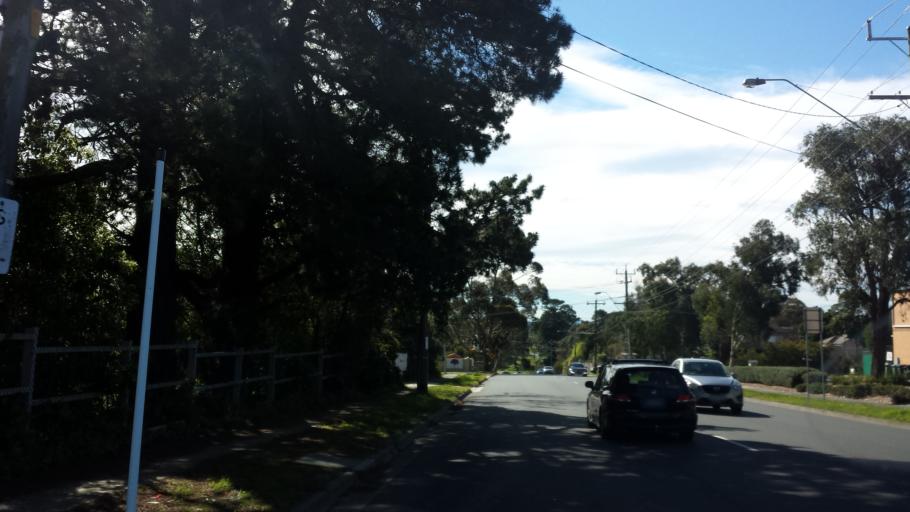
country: AU
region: Victoria
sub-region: Maroondah
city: Warranwood
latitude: -37.7908
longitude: 145.2358
